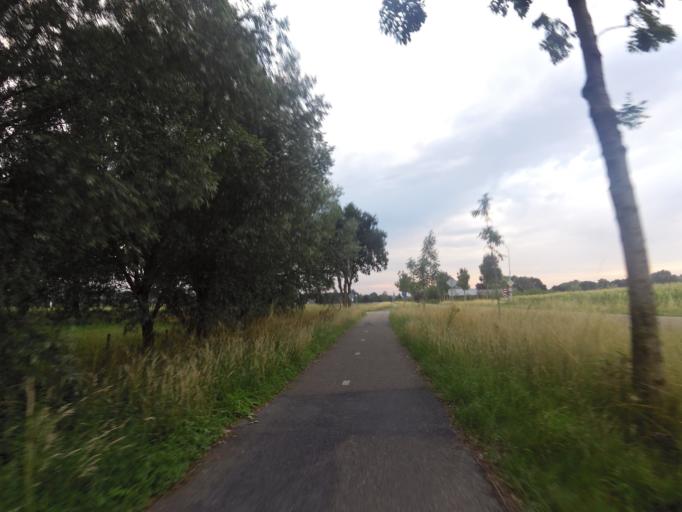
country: NL
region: Gelderland
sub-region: Oude IJsselstreek
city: Gendringen
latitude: 51.9106
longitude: 6.3518
